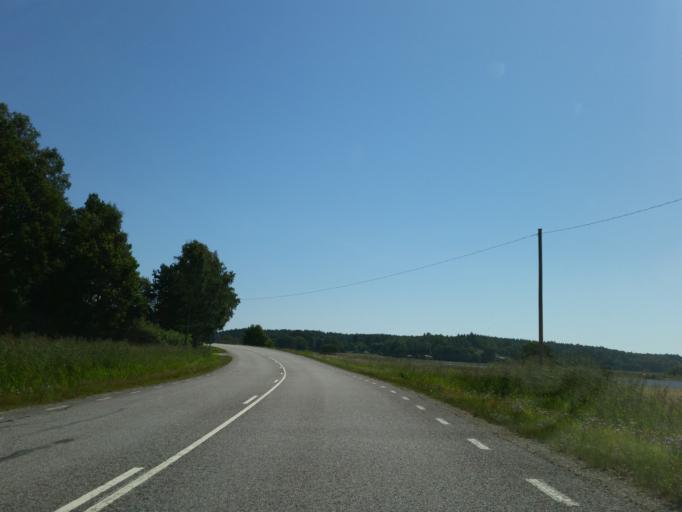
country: SE
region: Soedermanland
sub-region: Trosa Kommun
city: Vagnharad
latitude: 58.9917
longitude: 17.6174
